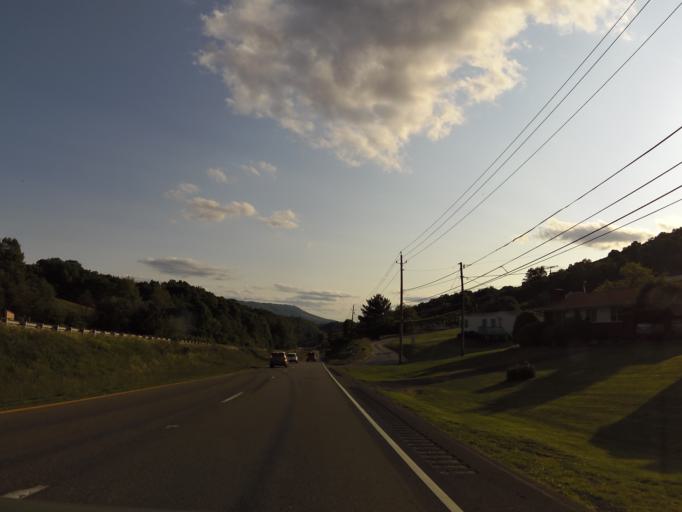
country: US
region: Virginia
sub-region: Russell County
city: Honaker
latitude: 36.9337
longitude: -81.9876
